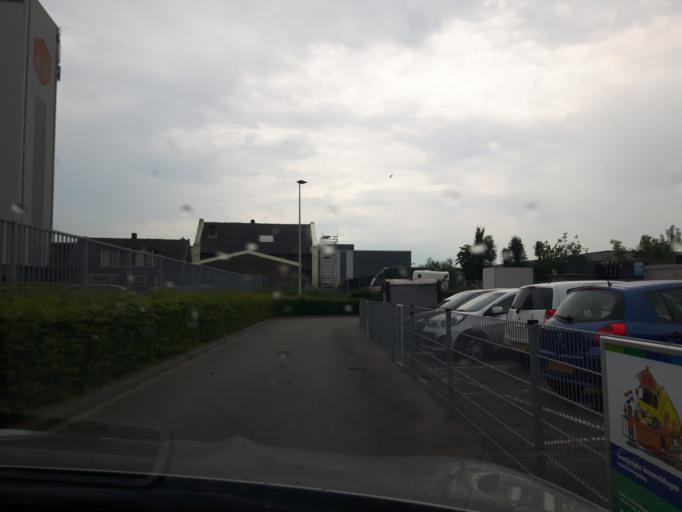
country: NL
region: Utrecht
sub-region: Gemeente Woerden
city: Woerden
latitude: 52.0838
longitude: 4.8659
